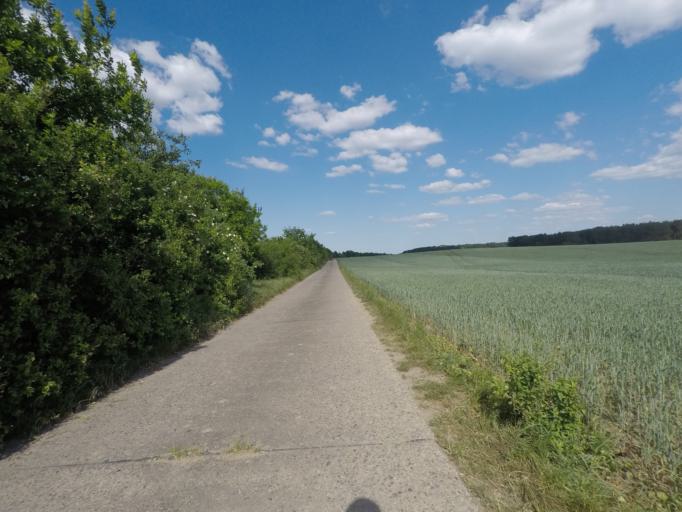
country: DE
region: Brandenburg
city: Melchow
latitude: 52.8679
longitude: 13.6966
